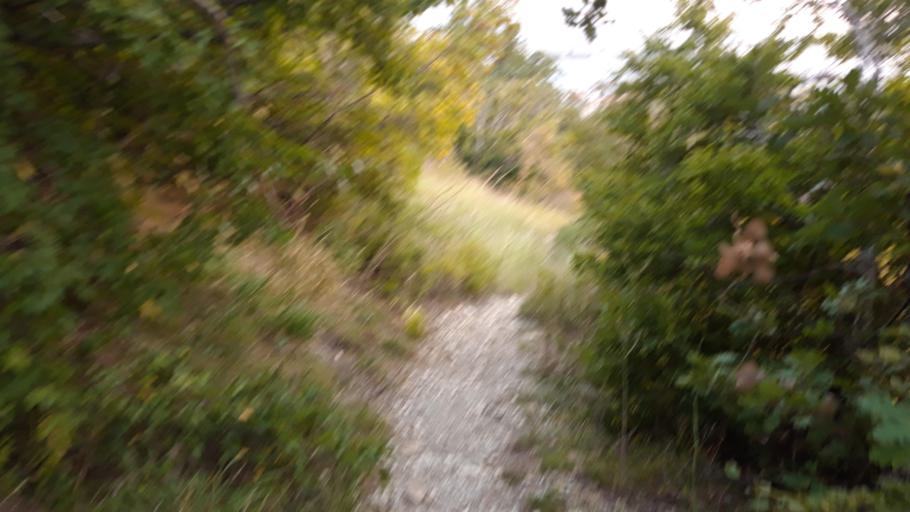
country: RU
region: Krasnodarskiy
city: Gelendzhik
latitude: 44.5827
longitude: 38.0869
